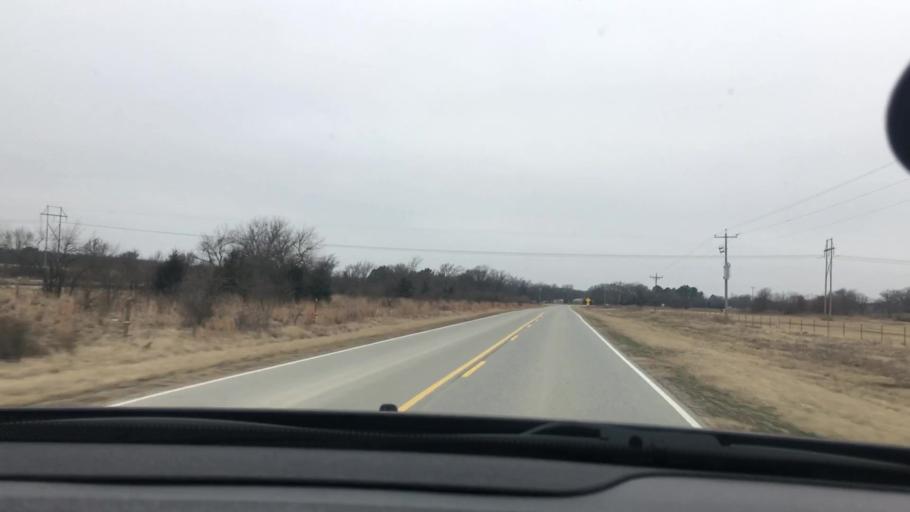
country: US
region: Oklahoma
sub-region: Coal County
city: Coalgate
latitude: 34.5079
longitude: -96.2984
